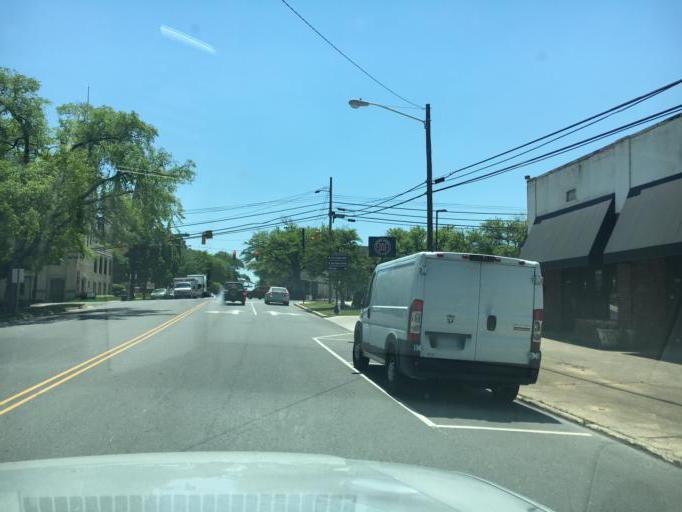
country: US
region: North Carolina
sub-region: Cleveland County
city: Shelby
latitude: 35.2941
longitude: -81.5401
